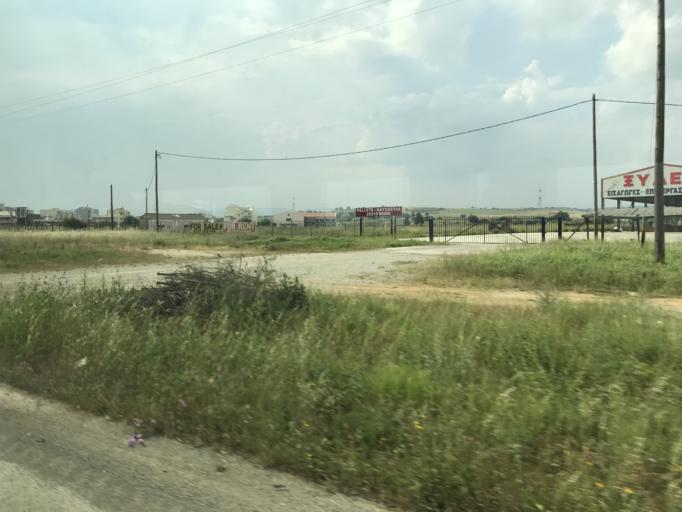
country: GR
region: East Macedonia and Thrace
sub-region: Nomos Evrou
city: Alexandroupoli
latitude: 40.8570
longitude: 25.9415
